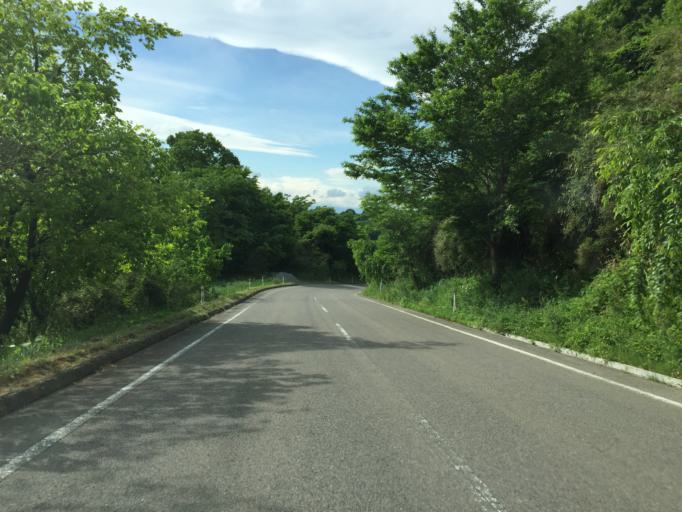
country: JP
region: Fukushima
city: Nihommatsu
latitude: 37.6114
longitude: 140.5253
